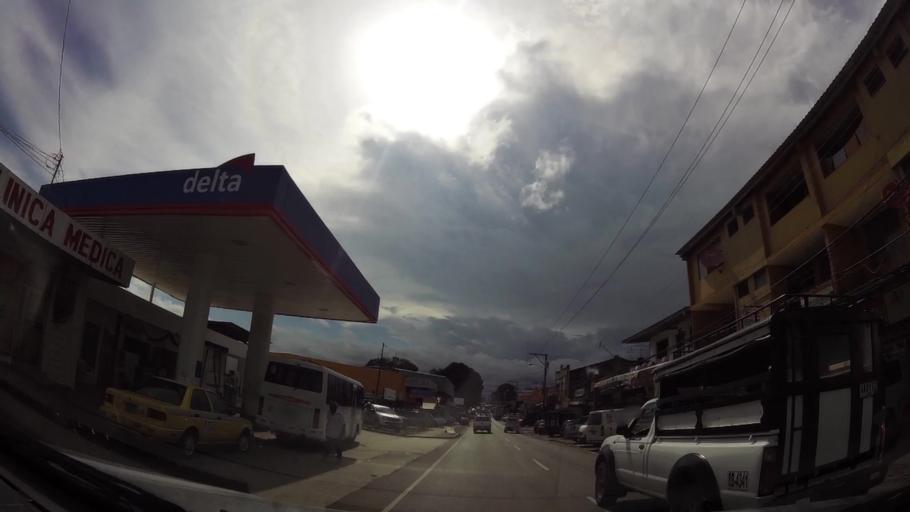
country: PA
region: Panama
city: La Chorrera
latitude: 8.8771
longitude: -79.7857
